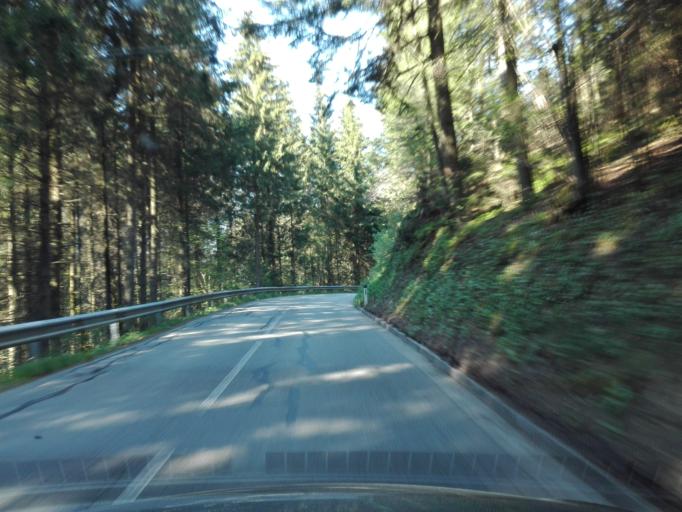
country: DE
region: Bavaria
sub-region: Lower Bavaria
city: Obernzell
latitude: 48.4933
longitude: 13.5780
